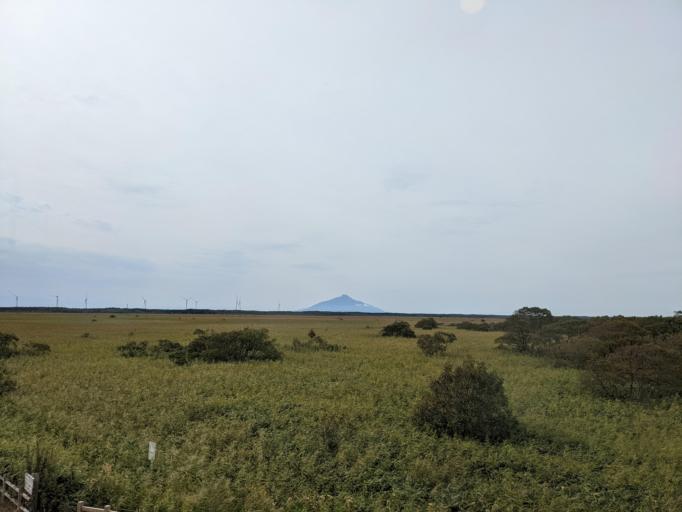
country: JP
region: Hokkaido
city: Makubetsu
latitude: 45.0102
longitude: 141.7307
